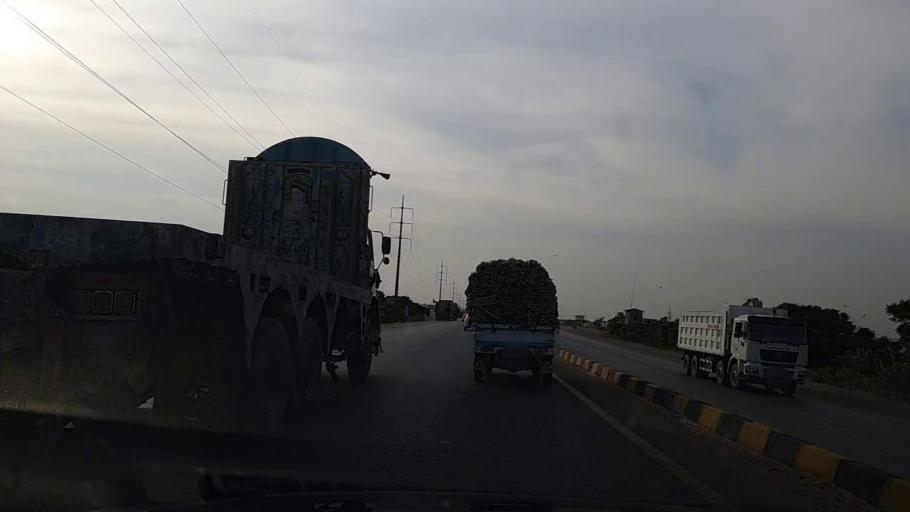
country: PK
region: Sindh
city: Gharo
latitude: 24.8373
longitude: 67.4488
